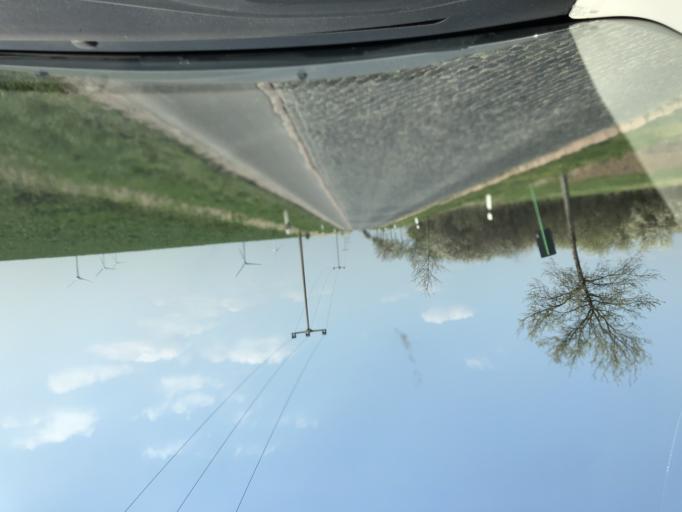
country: DE
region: Saxony-Anhalt
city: Landsberg
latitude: 51.5657
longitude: 12.1371
